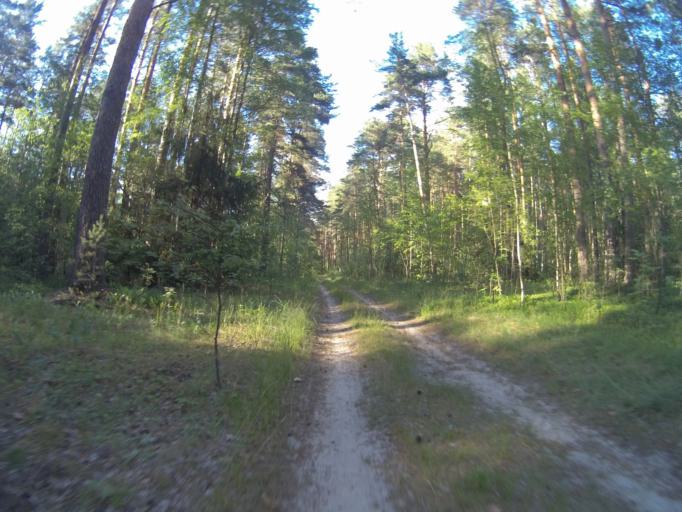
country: RU
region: Vladimir
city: Bogolyubovo
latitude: 56.1321
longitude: 40.5339
